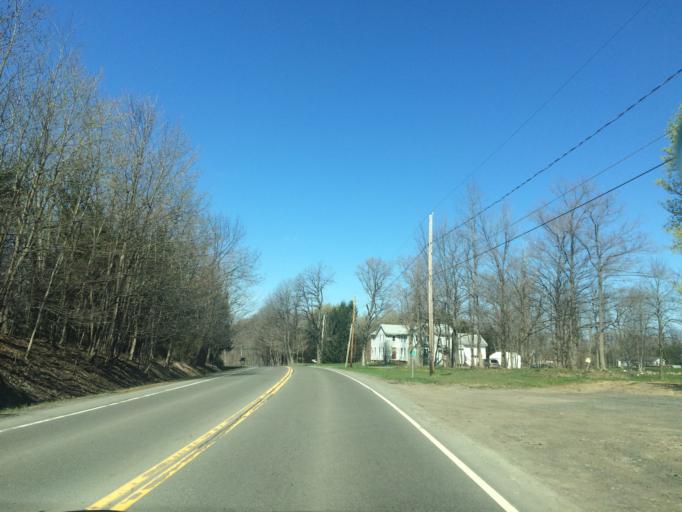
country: US
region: New York
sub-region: Wayne County
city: Macedon
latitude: 43.0959
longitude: -77.3623
